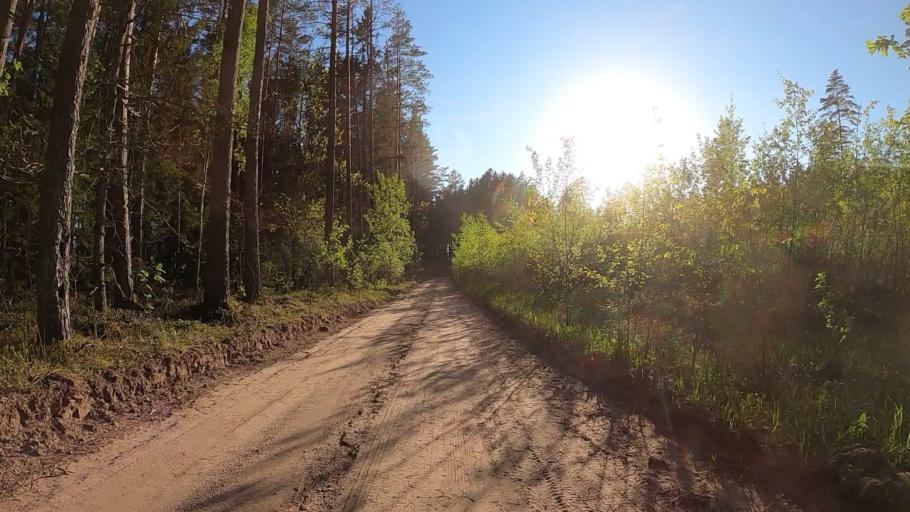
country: LV
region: Kekava
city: Kekava
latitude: 56.7591
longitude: 24.2667
